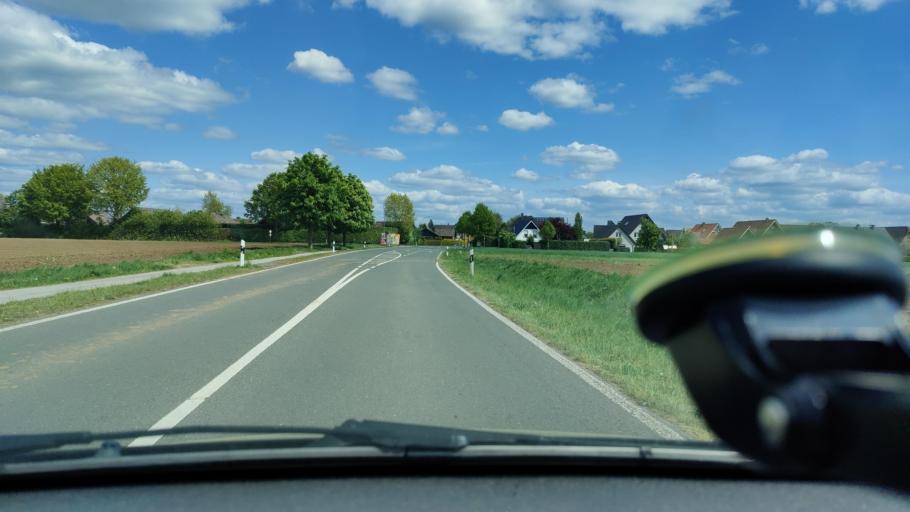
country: DE
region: North Rhine-Westphalia
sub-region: Regierungsbezirk Munster
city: Heiden
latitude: 51.8258
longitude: 6.9200
